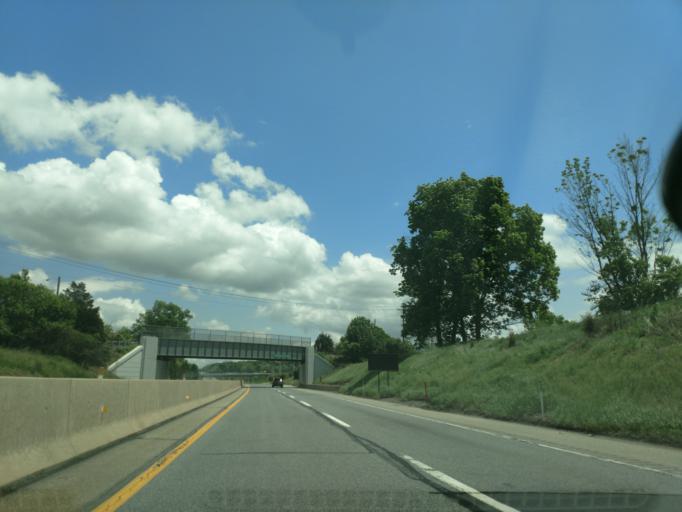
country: US
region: Pennsylvania
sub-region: Lancaster County
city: Swartzville
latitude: 40.2177
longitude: -76.0804
